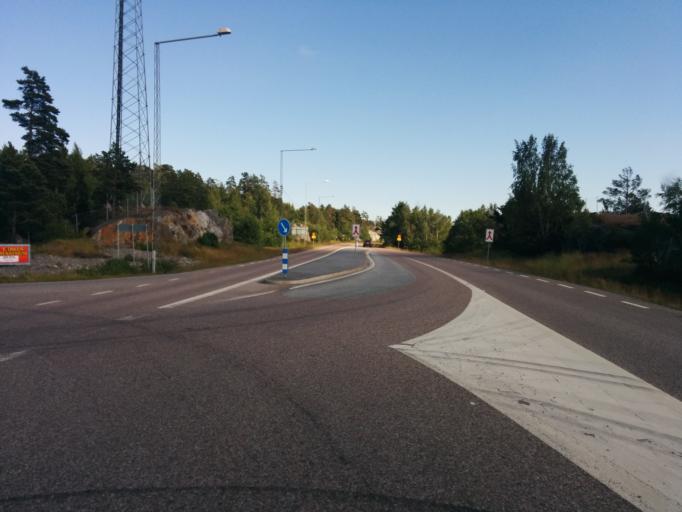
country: SE
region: Stockholm
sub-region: Varmdo Kommun
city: Gustavsberg
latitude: 59.3051
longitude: 18.3856
